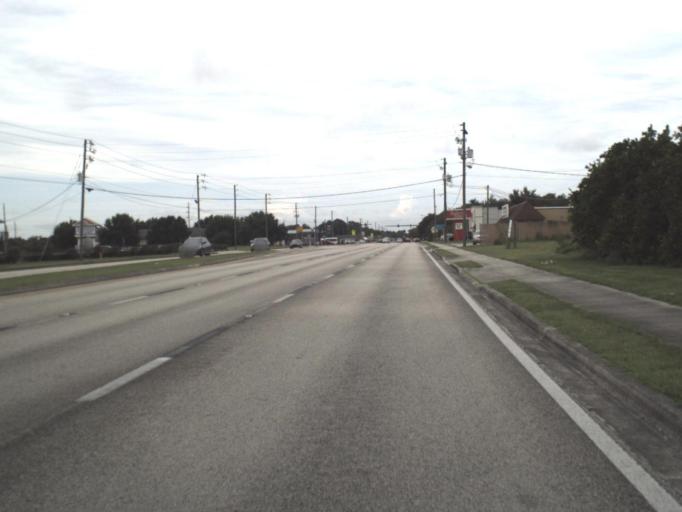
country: US
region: Florida
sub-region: Polk County
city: Eagle Lake
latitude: 27.9853
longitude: -81.7490
